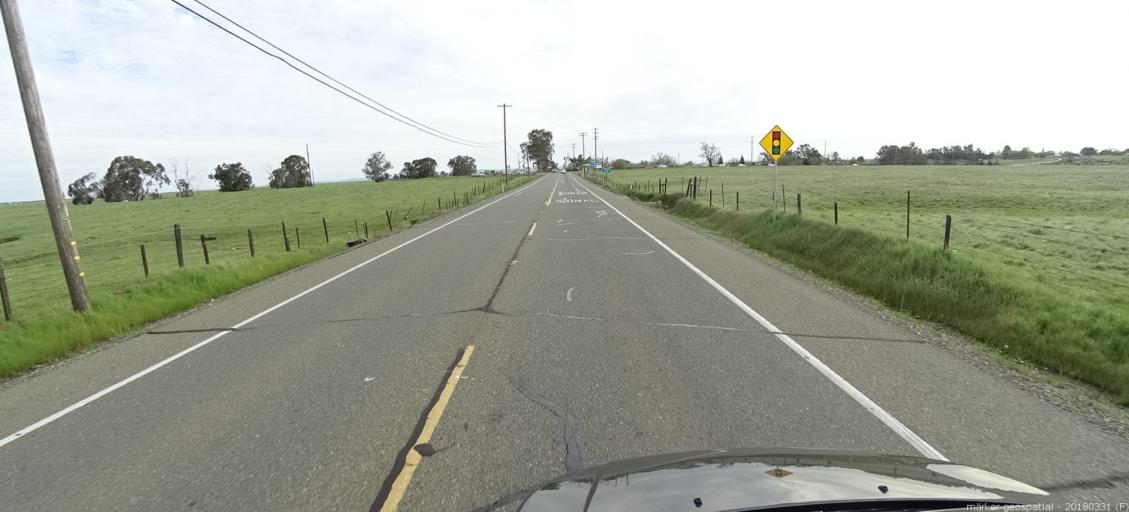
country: US
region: California
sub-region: Sacramento County
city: Wilton
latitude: 38.5001
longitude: -121.2254
